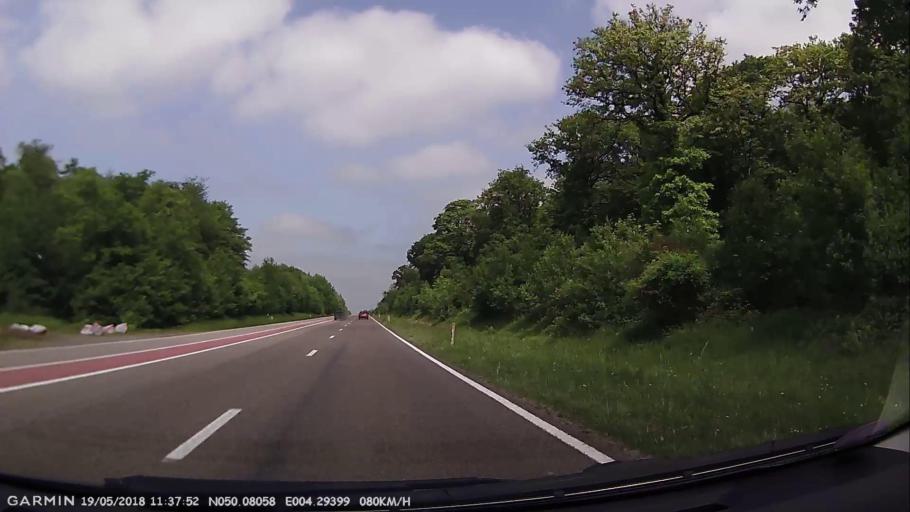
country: BE
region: Wallonia
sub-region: Province du Hainaut
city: Chimay
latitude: 50.0808
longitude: 4.2940
